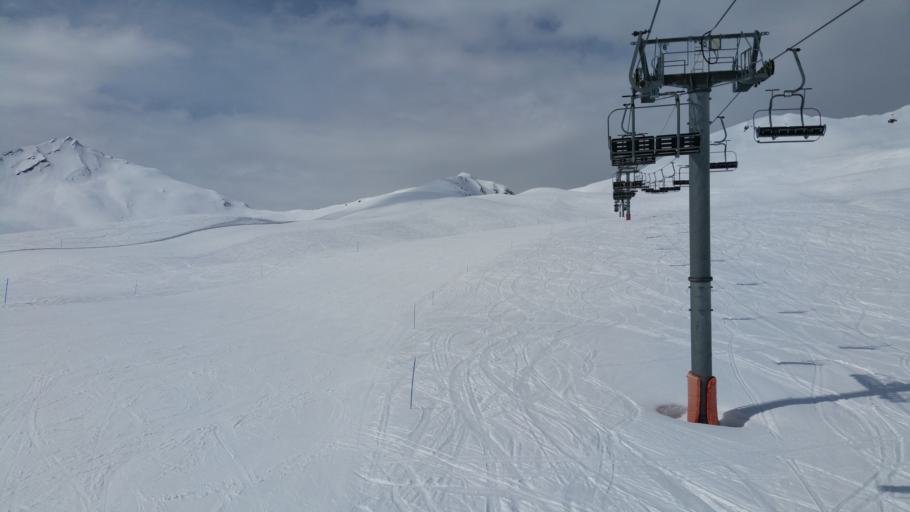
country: FR
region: Rhone-Alpes
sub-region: Departement de la Savoie
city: Valloire
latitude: 45.2003
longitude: 6.3976
